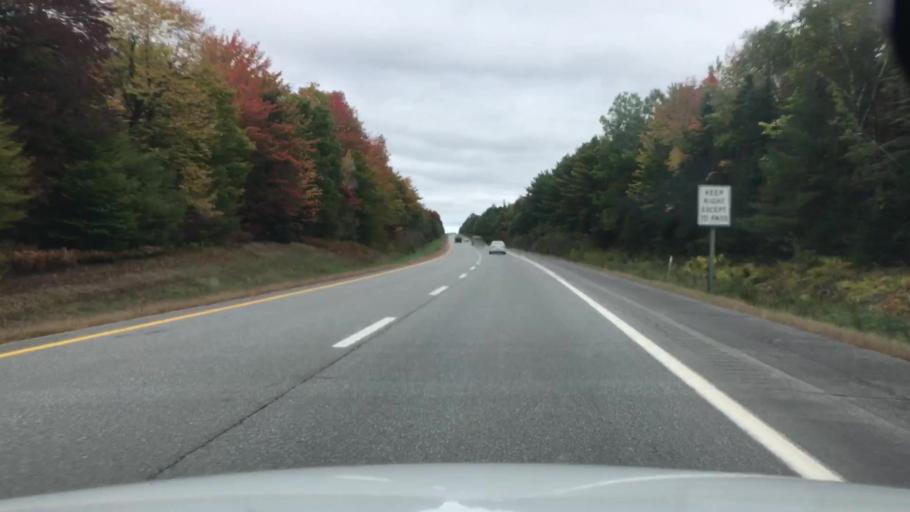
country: US
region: Maine
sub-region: Penobscot County
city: Plymouth
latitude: 44.7911
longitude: -69.1995
